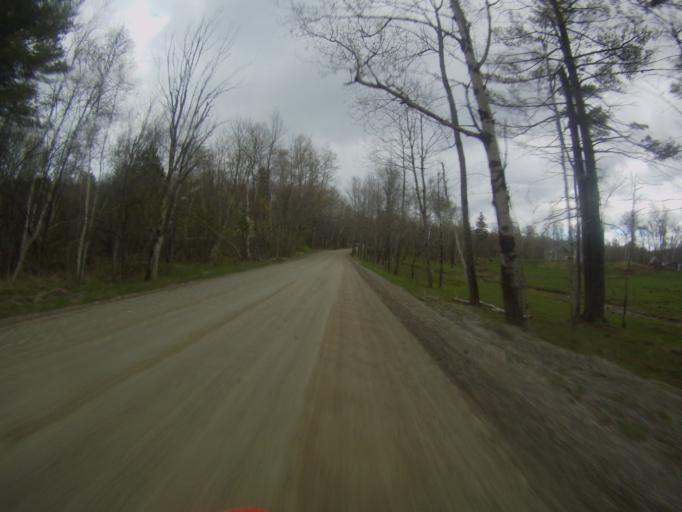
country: US
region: Vermont
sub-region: Addison County
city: Bristol
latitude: 44.0643
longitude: -73.0417
